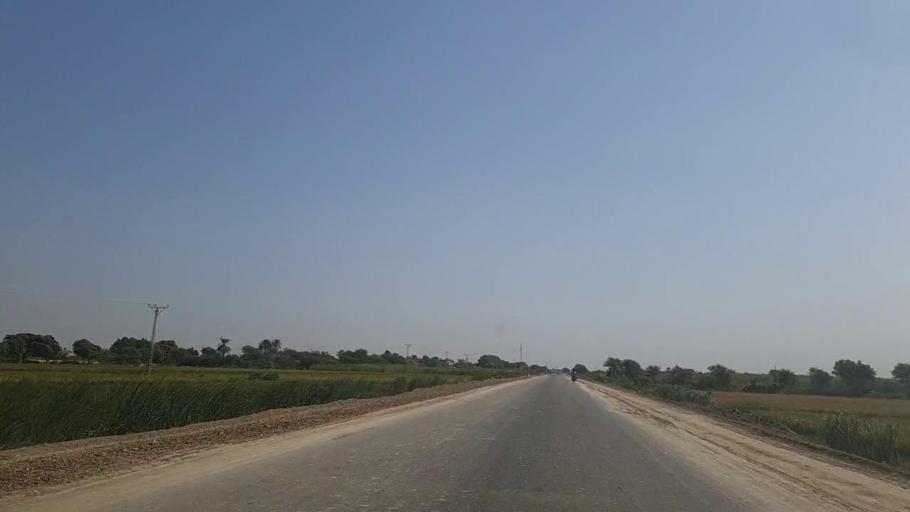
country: PK
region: Sindh
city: Mirpur Batoro
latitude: 24.7458
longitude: 68.2423
